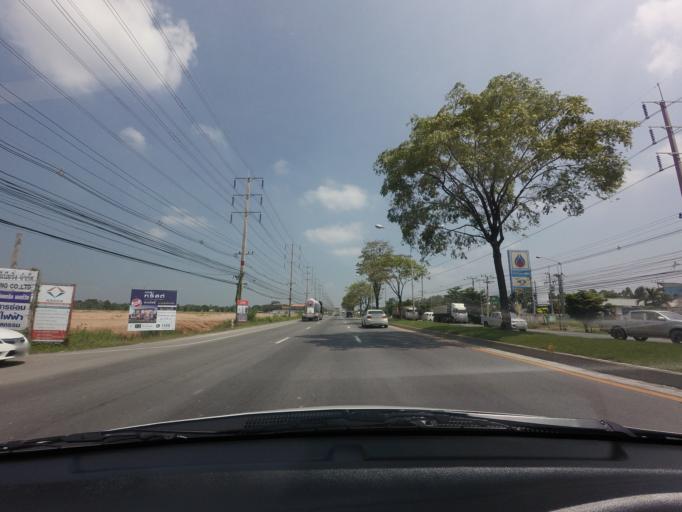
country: TH
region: Chachoengsao
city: Bang Pakong
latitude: 13.5932
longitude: 101.0147
